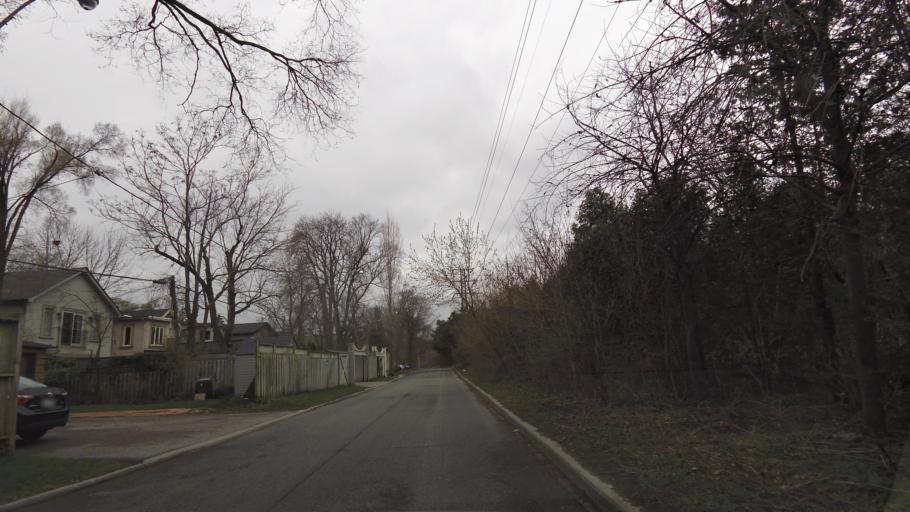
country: CA
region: Ontario
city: Toronto
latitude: 43.6849
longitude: -79.3812
